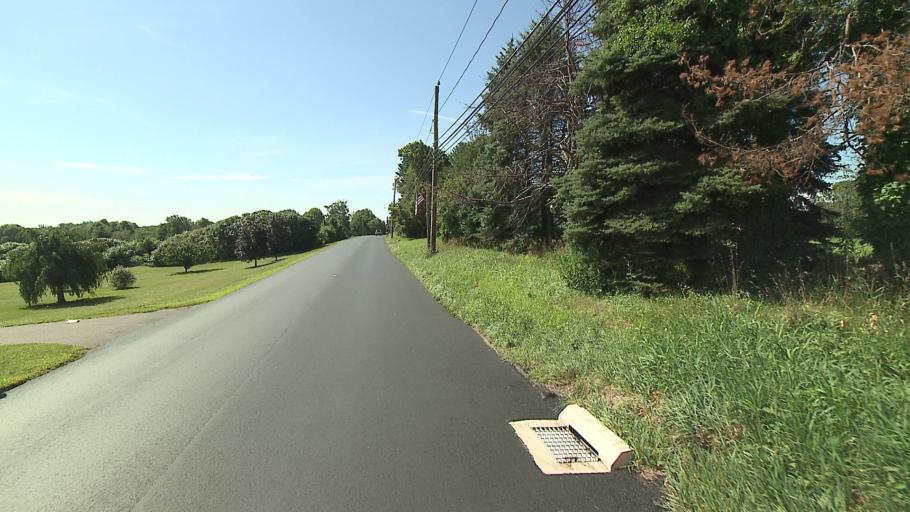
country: US
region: Connecticut
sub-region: Hartford County
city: Tariffville
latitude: 41.9480
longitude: -72.7242
